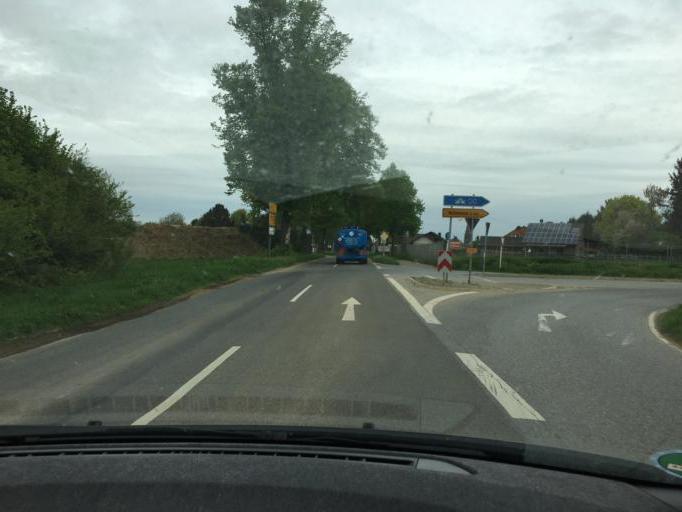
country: DE
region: North Rhine-Westphalia
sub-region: Regierungsbezirk Koln
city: Titz
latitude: 51.0906
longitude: 6.4154
